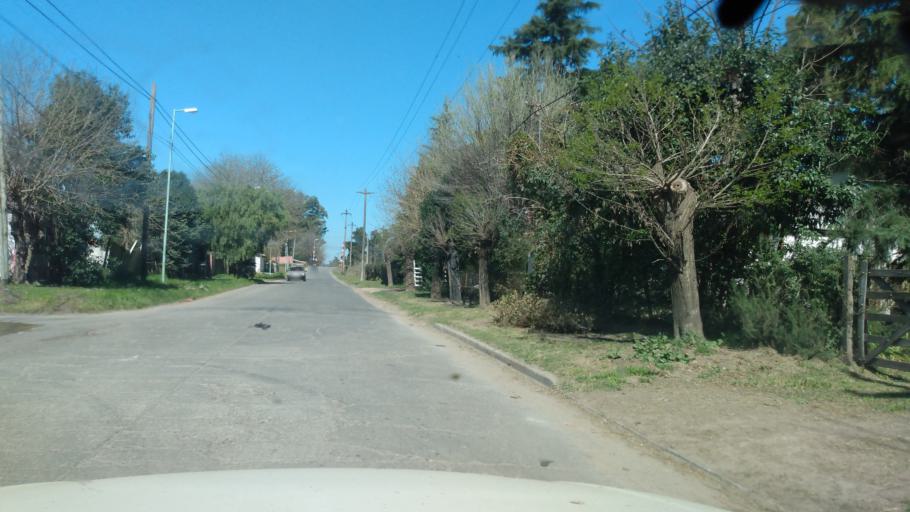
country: AR
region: Buenos Aires
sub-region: Partido de Lujan
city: Lujan
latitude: -34.5816
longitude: -59.1215
